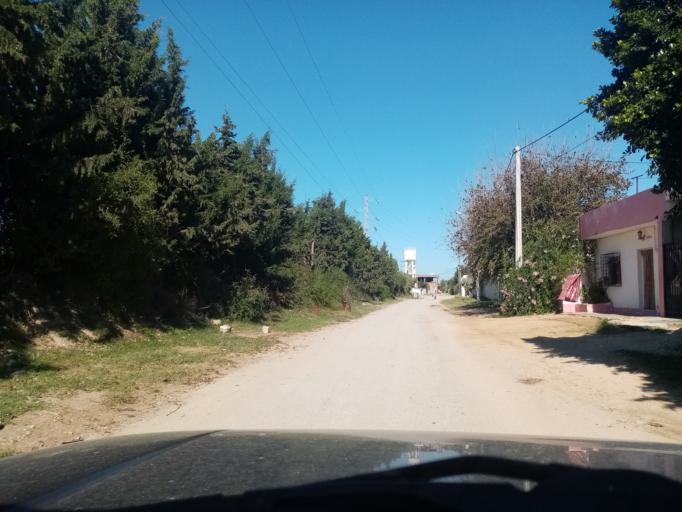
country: TN
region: Nabul
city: Bu `Urqub
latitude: 36.5732
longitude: 10.5739
